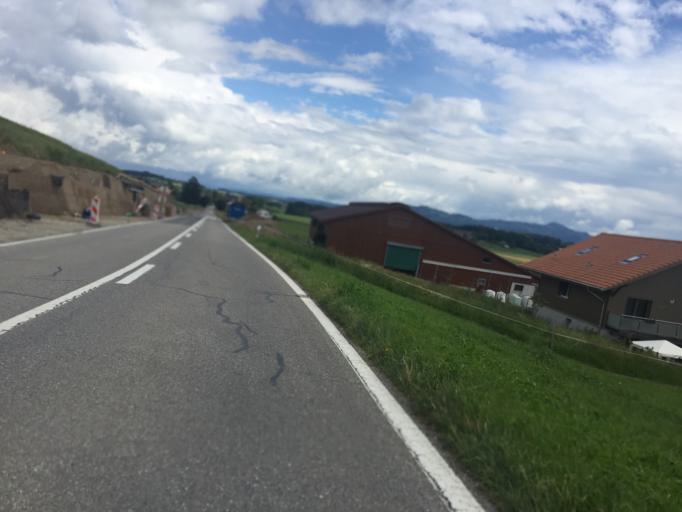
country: CH
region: Bern
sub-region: Bern-Mittelland District
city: Kirchlindach
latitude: 46.9878
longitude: 7.3932
